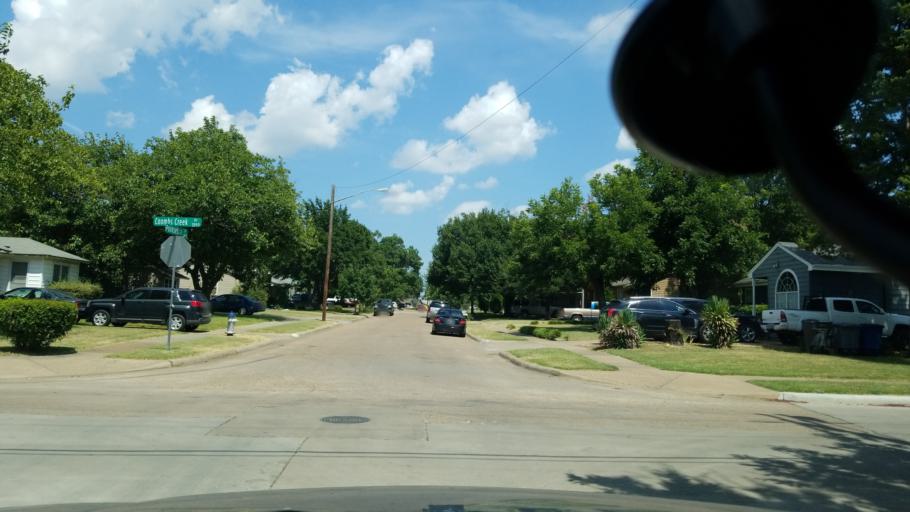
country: US
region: Texas
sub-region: Dallas County
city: Cockrell Hill
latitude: 32.7247
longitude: -96.8777
